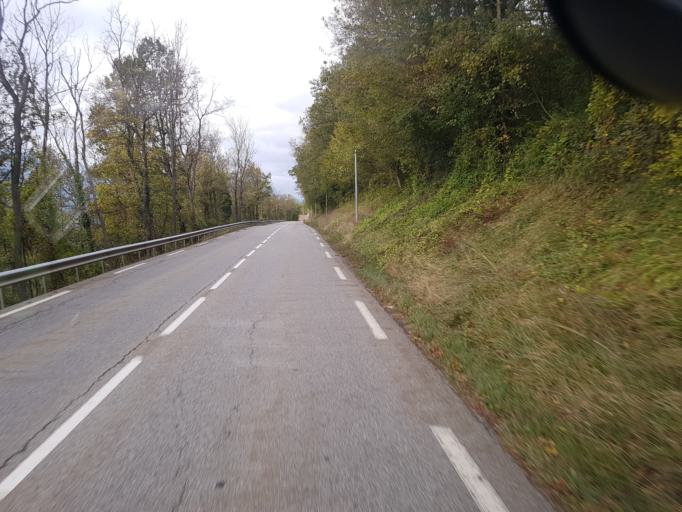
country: FR
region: Rhone-Alpes
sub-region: Departement de l'Isere
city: Le Gua
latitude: 44.9763
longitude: 5.6437
